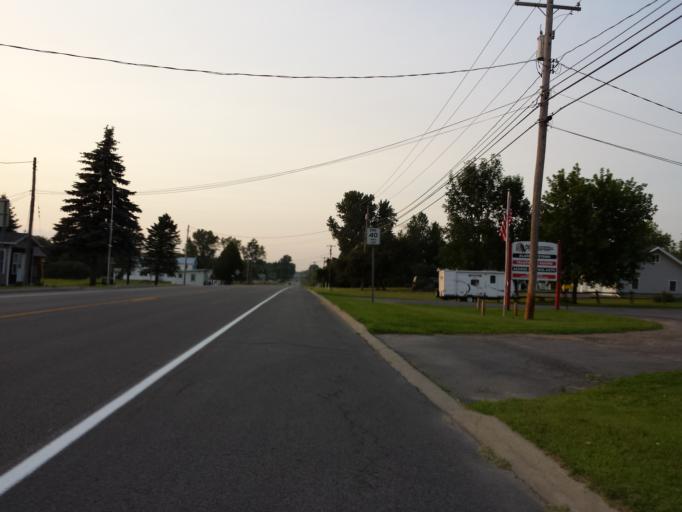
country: US
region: New York
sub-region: St. Lawrence County
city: Potsdam
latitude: 44.6984
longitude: -74.9871
